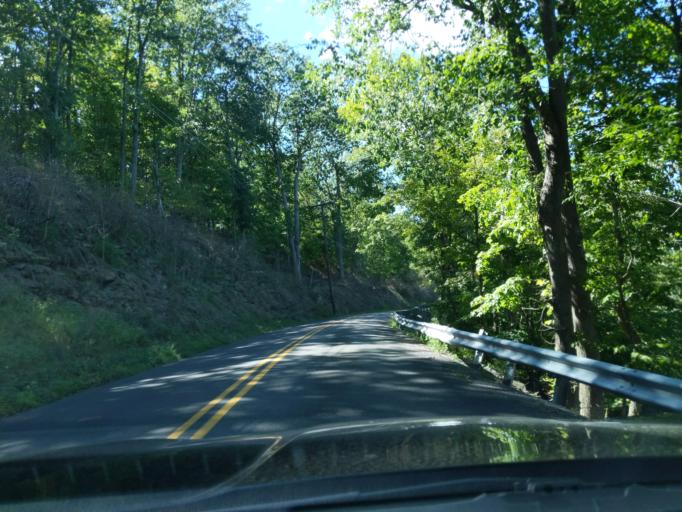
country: US
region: Pennsylvania
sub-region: Blair County
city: Williamsburg
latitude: 40.4755
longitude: -78.2842
